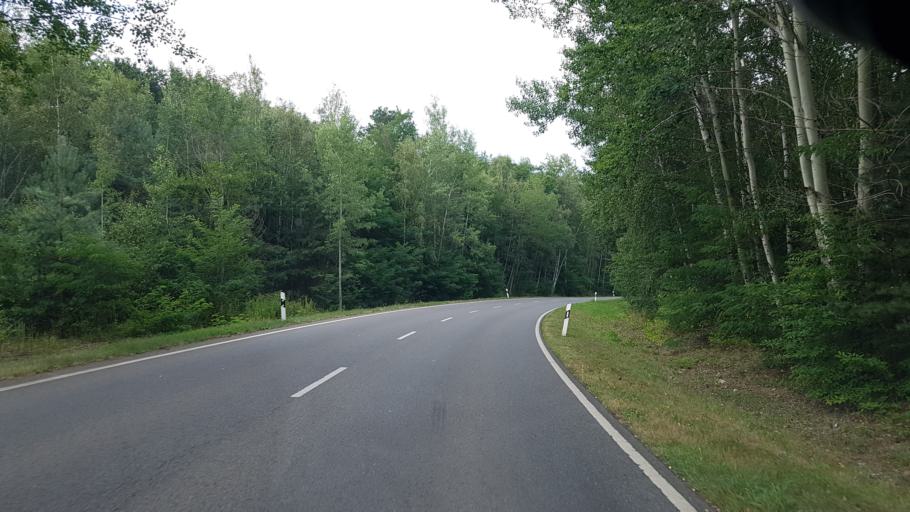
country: DE
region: Brandenburg
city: Lauchhammer
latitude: 51.4968
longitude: 13.7390
